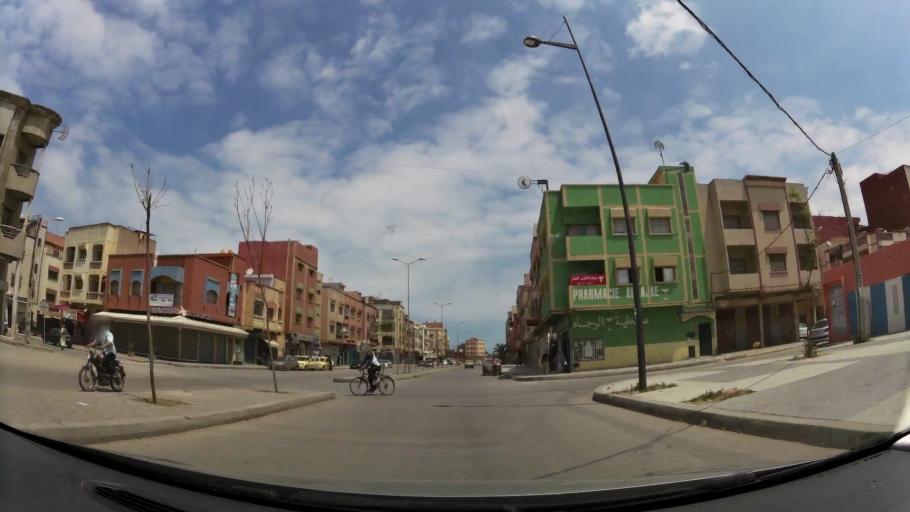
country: MA
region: Rabat-Sale-Zemmour-Zaer
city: Sale
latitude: 34.0568
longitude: -6.7829
